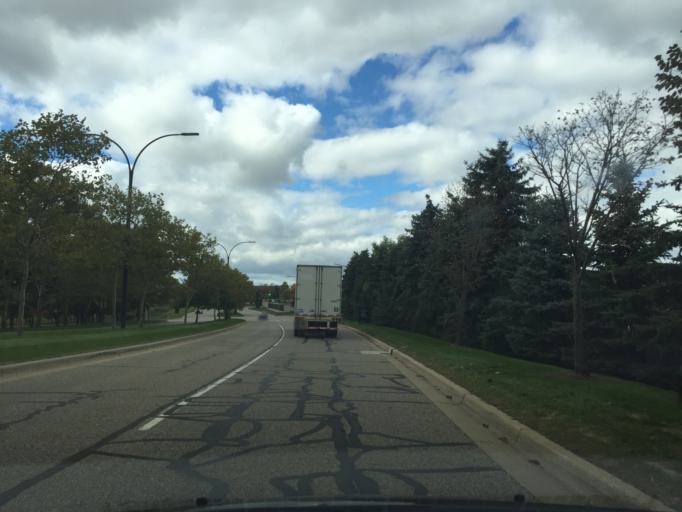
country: US
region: Michigan
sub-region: Oakland County
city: Auburn Hills
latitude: 42.6515
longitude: -83.2228
